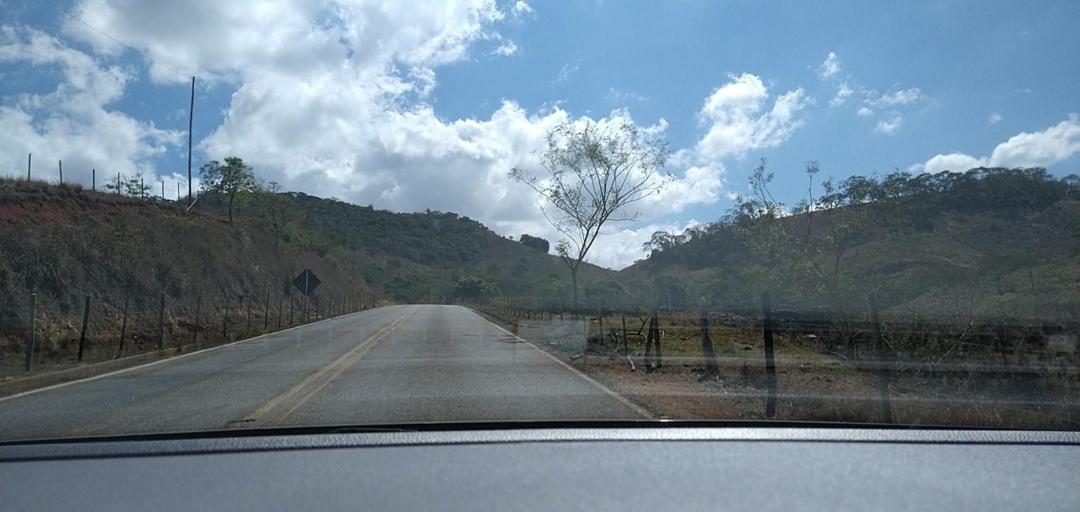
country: BR
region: Minas Gerais
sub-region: Ponte Nova
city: Ponte Nova
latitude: -20.2770
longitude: -42.9018
